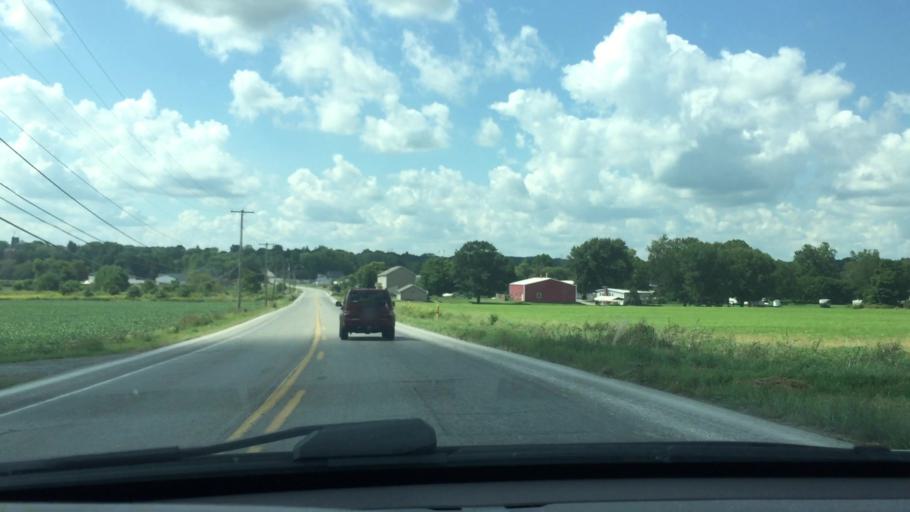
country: US
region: Pennsylvania
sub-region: Lawrence County
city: New Wilmington
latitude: 41.1226
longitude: -80.3165
